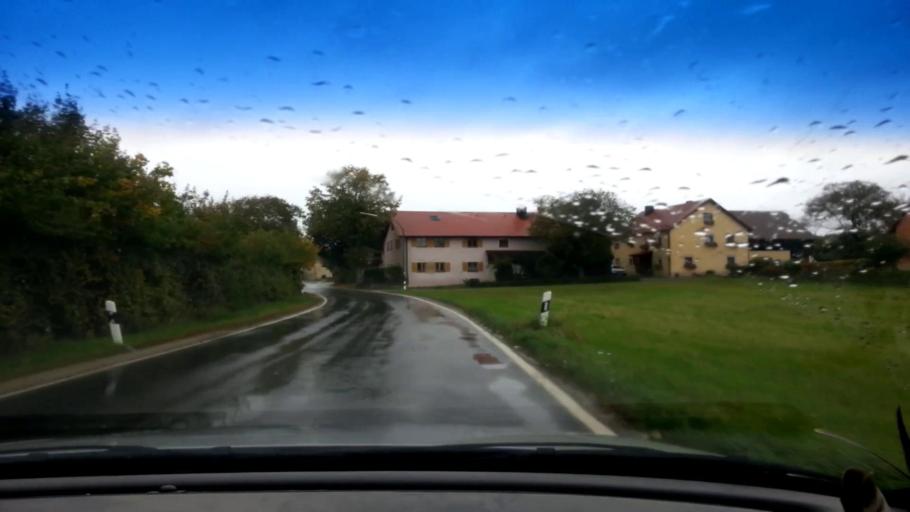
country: DE
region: Bavaria
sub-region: Upper Franconia
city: Poxdorf
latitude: 49.9352
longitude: 11.0803
